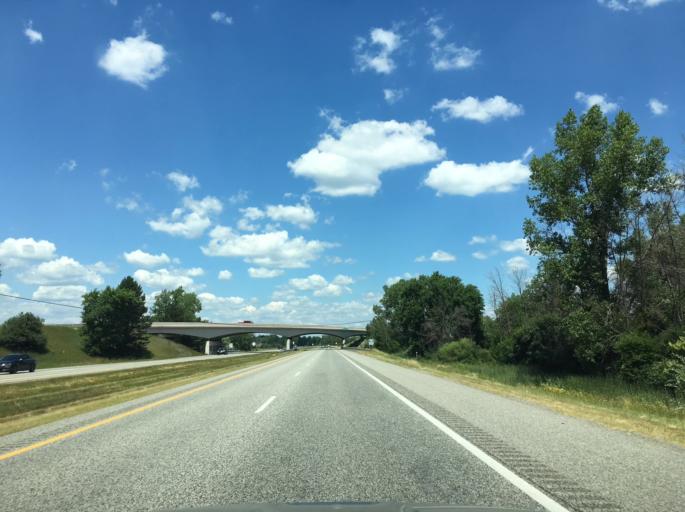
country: US
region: Michigan
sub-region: Midland County
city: Midland
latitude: 43.6387
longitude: -84.1859
